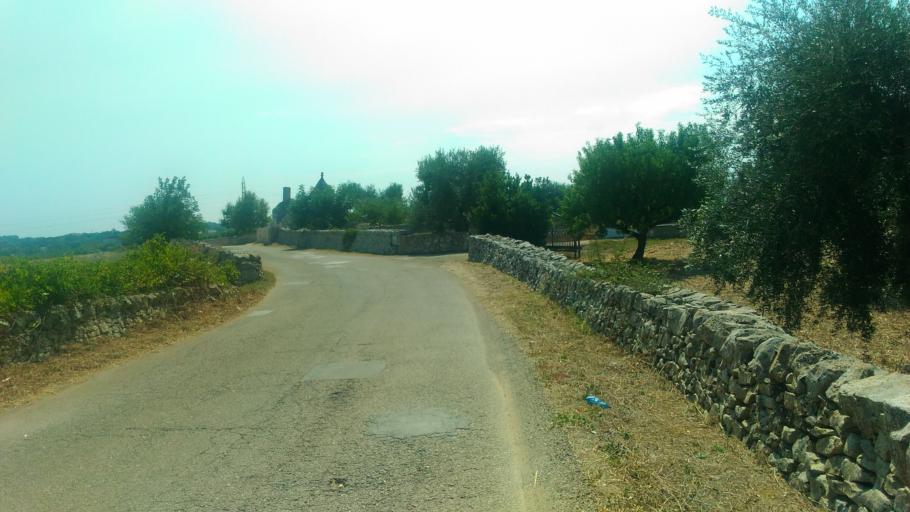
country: IT
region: Apulia
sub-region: Provincia di Brindisi
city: Cisternino
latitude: 40.7456
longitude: 17.3781
